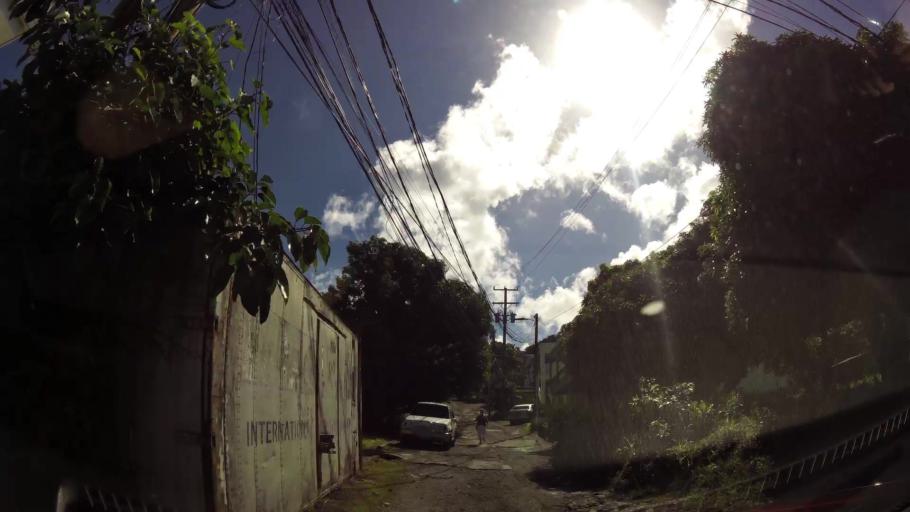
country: DM
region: Saint John
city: Portsmouth
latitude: 15.5550
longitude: -61.4568
